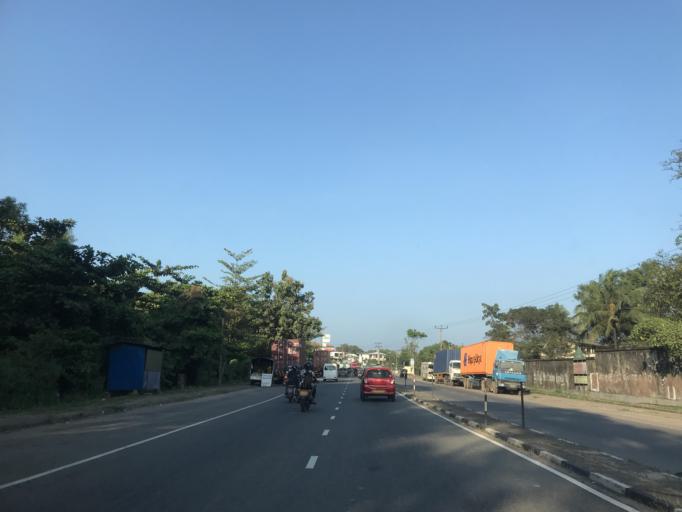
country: LK
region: Western
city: Ja Ela
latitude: 7.0994
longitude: 79.9089
